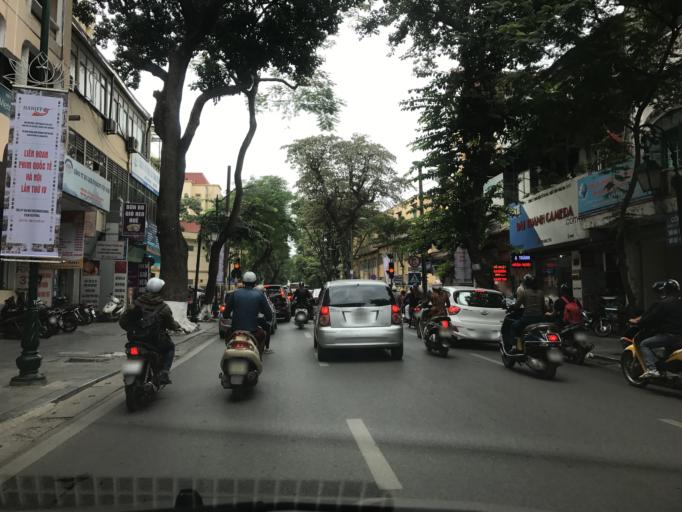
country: VN
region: Ha Noi
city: Hoan Kiem
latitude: 21.0268
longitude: 105.8483
